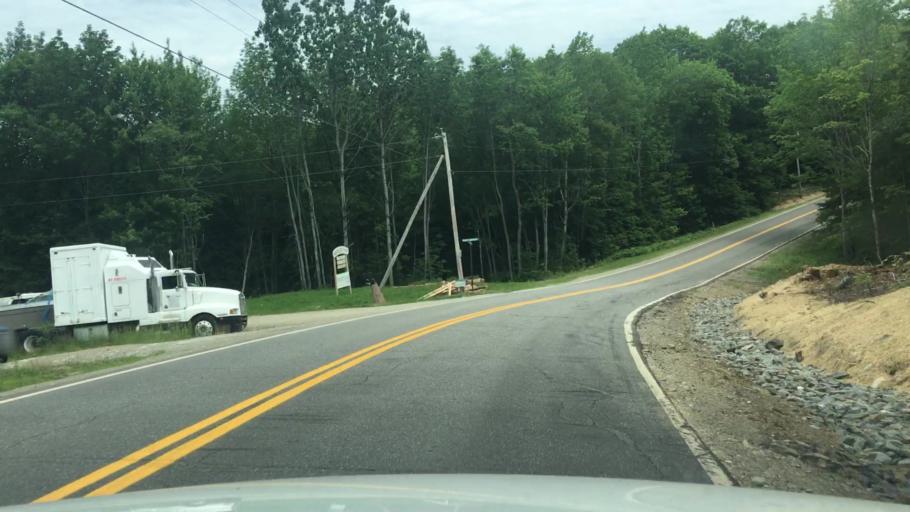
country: US
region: Maine
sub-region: Waldo County
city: Searsmont
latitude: 44.4568
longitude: -69.2714
